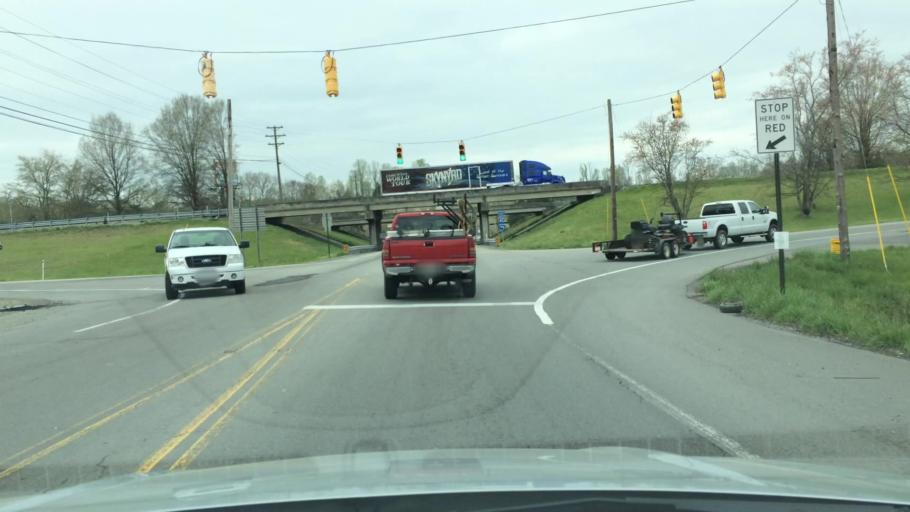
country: US
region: Tennessee
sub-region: Putnam County
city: Baxter
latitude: 36.1388
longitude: -85.6289
